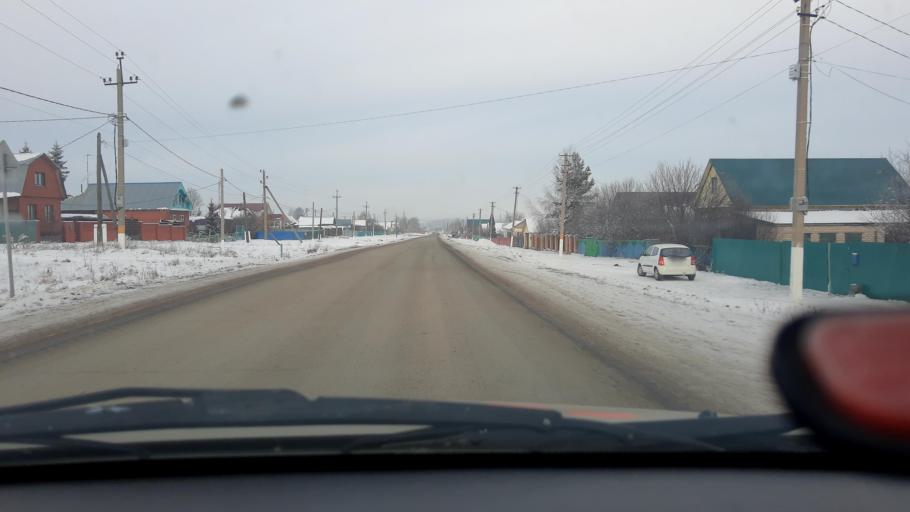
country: RU
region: Bashkortostan
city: Avdon
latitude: 54.4117
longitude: 55.8062
